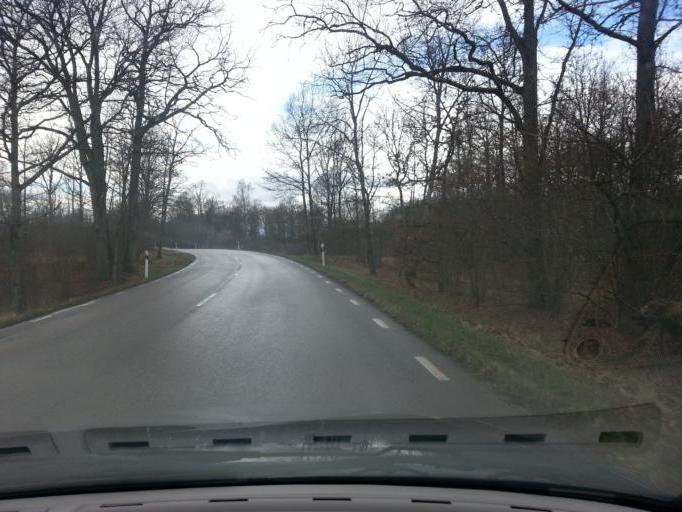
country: SE
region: Skane
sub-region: Klippans Kommun
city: Ljungbyhed
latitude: 56.0802
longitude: 13.2541
